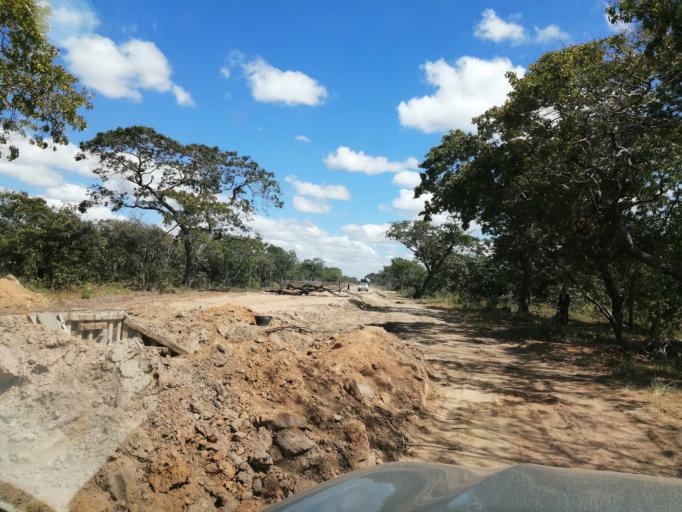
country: ZM
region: Central
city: Mumbwa
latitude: -14.5766
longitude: 27.2539
